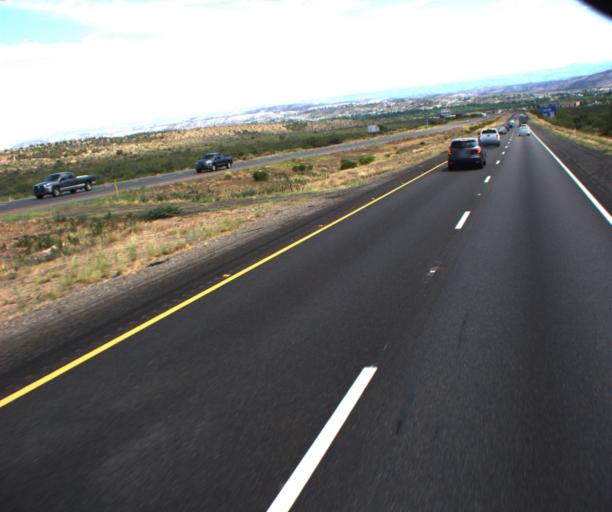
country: US
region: Arizona
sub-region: Yavapai County
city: Camp Verde
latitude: 34.5673
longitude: -111.8964
